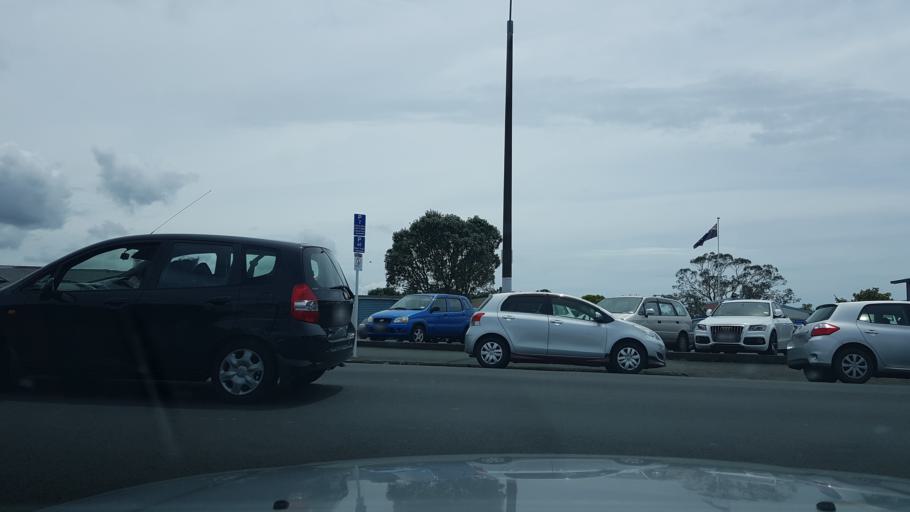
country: NZ
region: Auckland
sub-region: Auckland
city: North Shore
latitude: -36.8119
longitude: 174.7225
